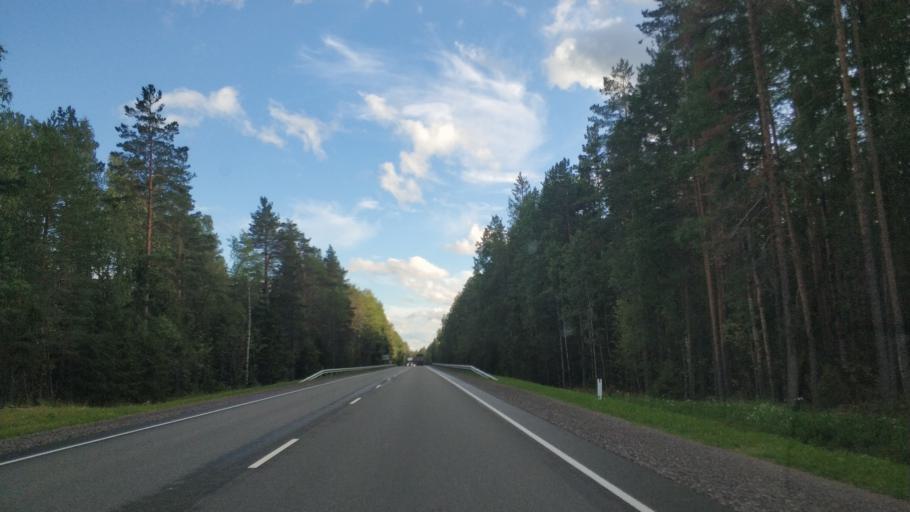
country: RU
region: Leningrad
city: Priozersk
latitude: 60.9004
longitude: 30.1599
